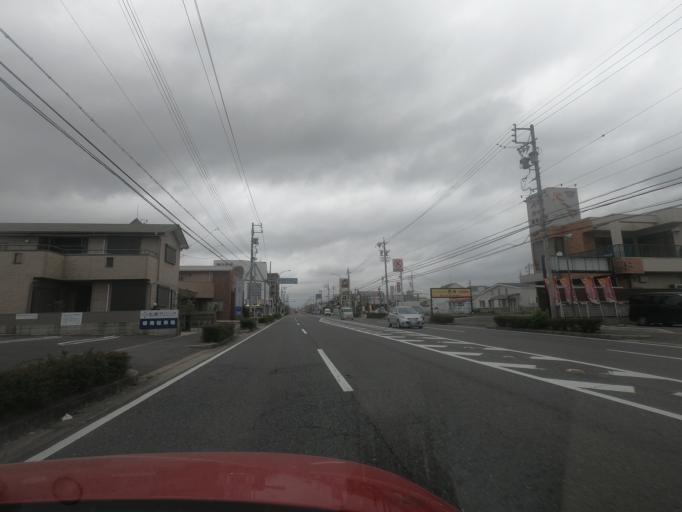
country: JP
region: Aichi
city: Kasugai
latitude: 35.2571
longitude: 136.9685
